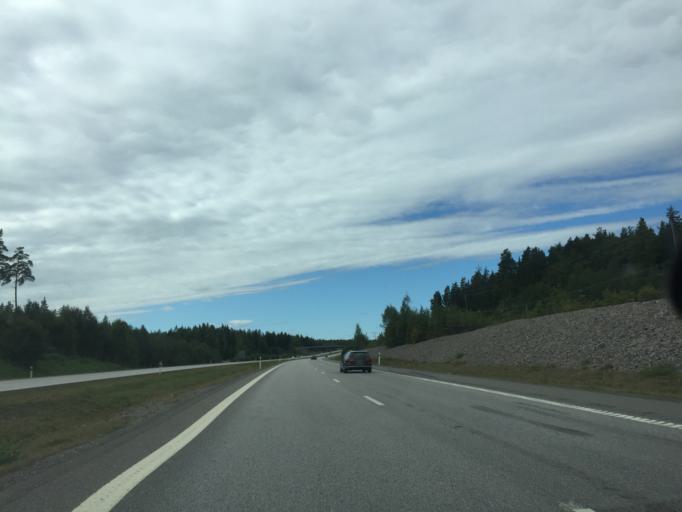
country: SE
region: OErebro
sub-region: Lindesbergs Kommun
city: Fellingsbro
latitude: 59.3780
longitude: 15.6397
